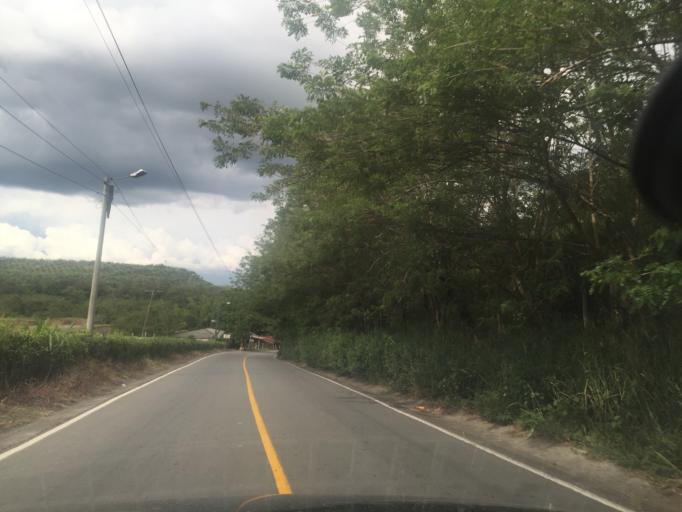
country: CO
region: Valle del Cauca
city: Caicedonia
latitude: 4.3402
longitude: -75.8550
